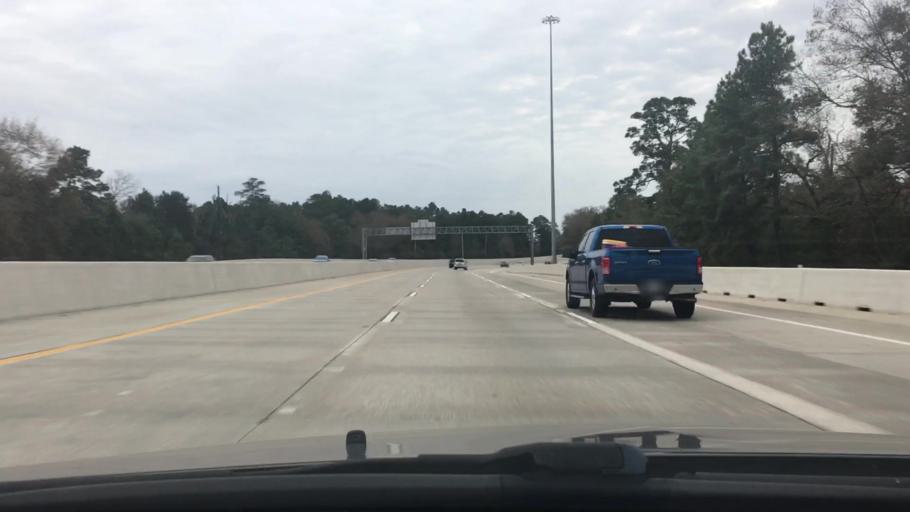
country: US
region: Texas
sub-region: Harris County
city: Spring
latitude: 30.0811
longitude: -95.4112
